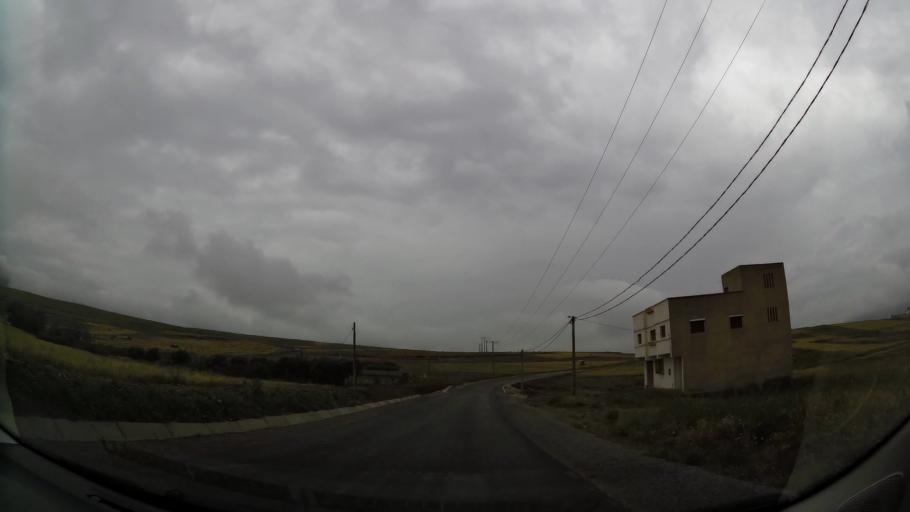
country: MA
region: Oriental
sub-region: Nador
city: Nador
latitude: 35.1522
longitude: -3.0312
